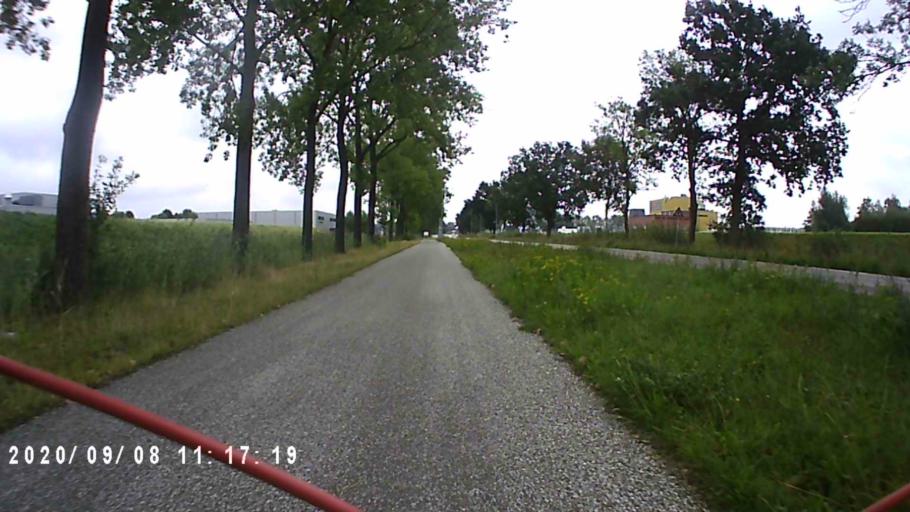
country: NL
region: Groningen
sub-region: Gemeente Hoogezand-Sappemeer
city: Hoogezand
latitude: 53.1704
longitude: 6.7359
